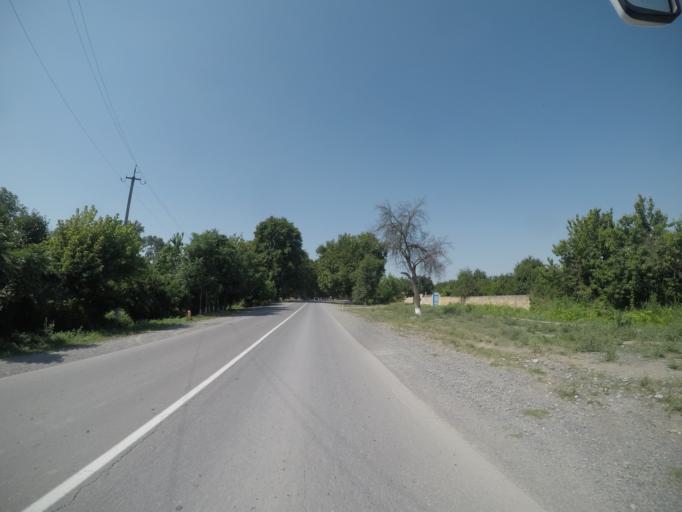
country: AZ
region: Agdas
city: Agdas
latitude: 40.6779
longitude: 47.5267
